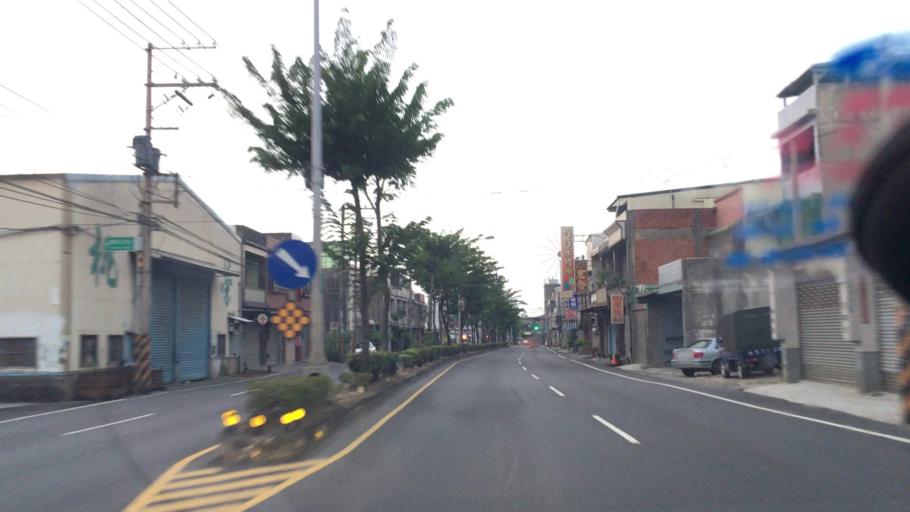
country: TW
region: Taiwan
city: Taoyuan City
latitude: 25.0596
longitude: 121.2674
